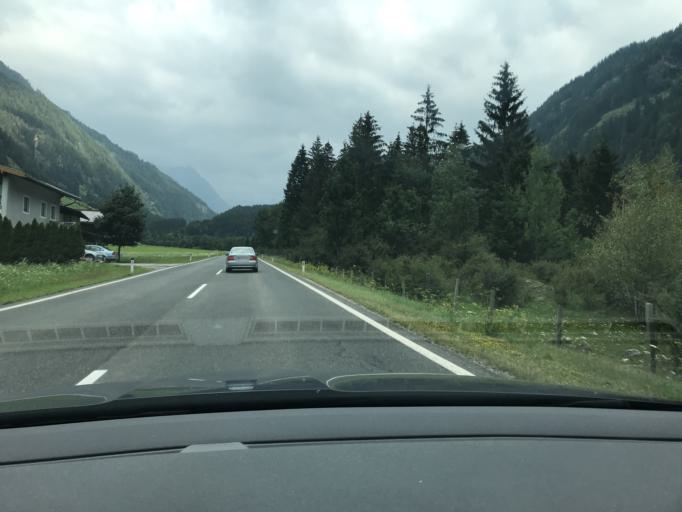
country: AT
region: Tyrol
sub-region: Politischer Bezirk Lienz
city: Hopfgarten in Defereggen
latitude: 46.9510
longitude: 12.5633
